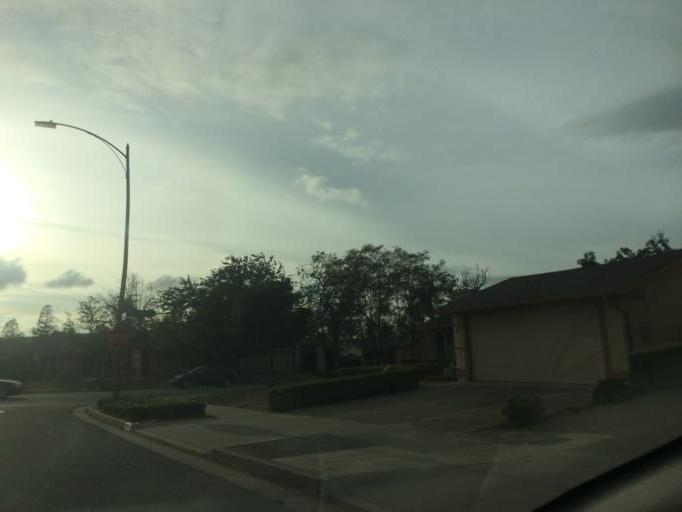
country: US
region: California
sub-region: Santa Clara County
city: Milpitas
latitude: 37.3959
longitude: -121.8827
